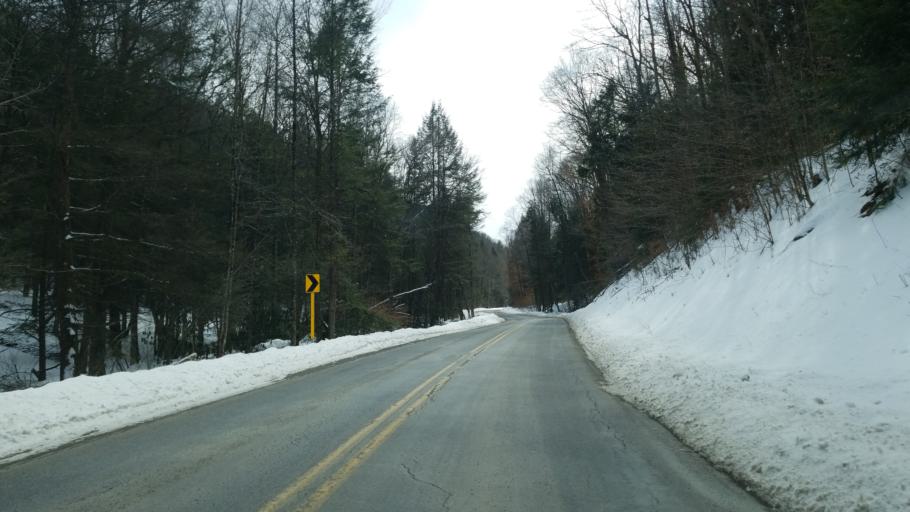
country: US
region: Pennsylvania
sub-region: Clearfield County
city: Shiloh
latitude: 41.2607
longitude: -78.1524
